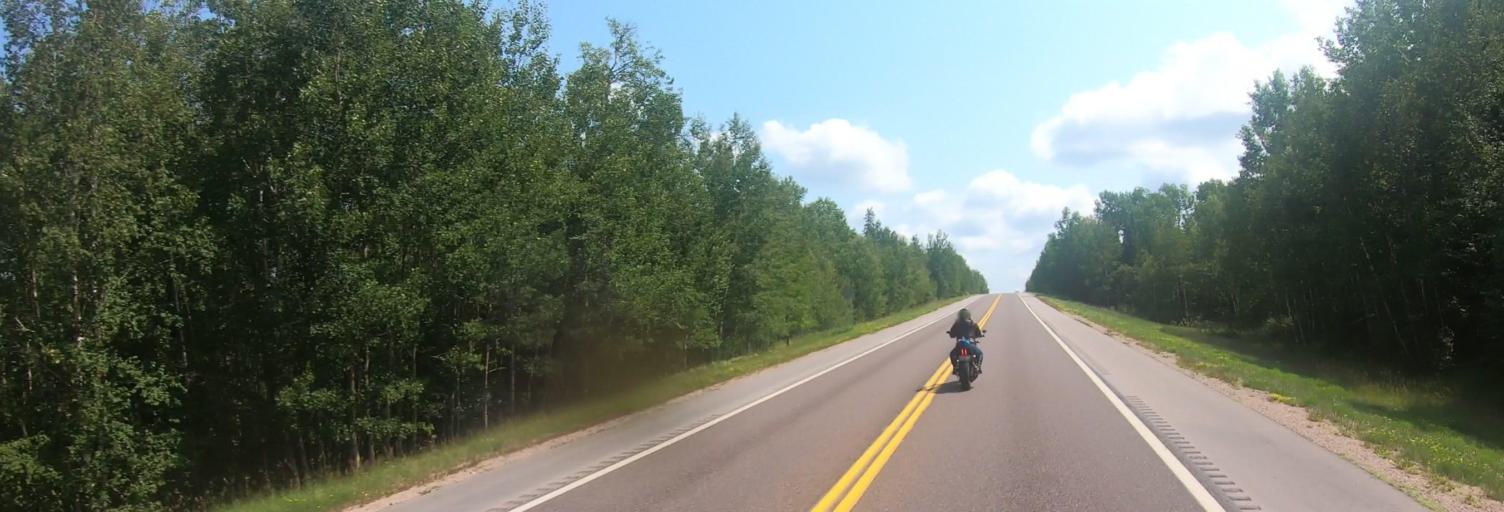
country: US
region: Minnesota
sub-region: Saint Louis County
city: Mountain Iron
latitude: 48.0749
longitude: -92.6732
